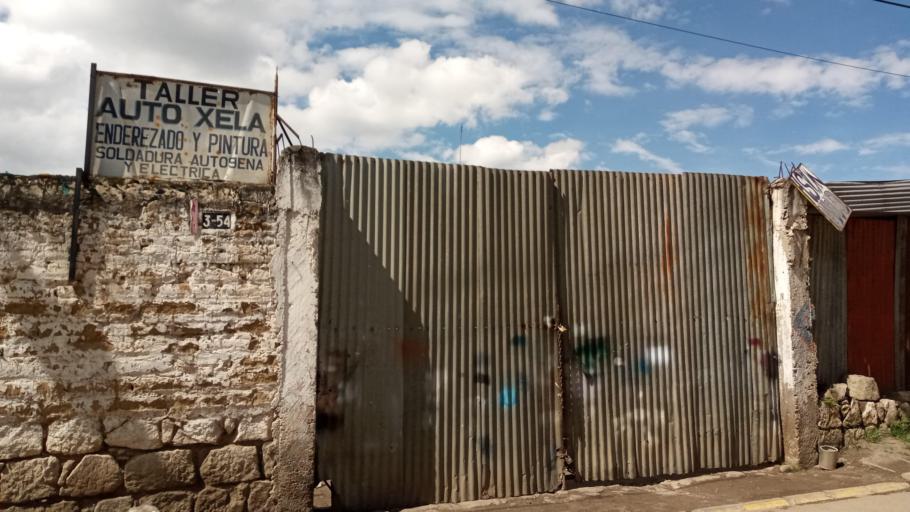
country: GT
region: Quetzaltenango
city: Quetzaltenango
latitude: 14.8411
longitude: -91.5091
